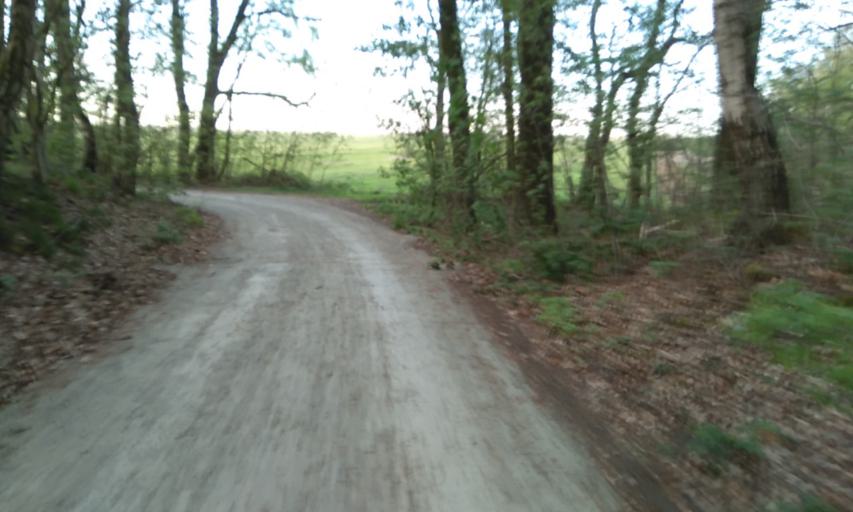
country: DE
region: Lower Saxony
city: Nottensdorf
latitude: 53.4921
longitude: 9.6145
